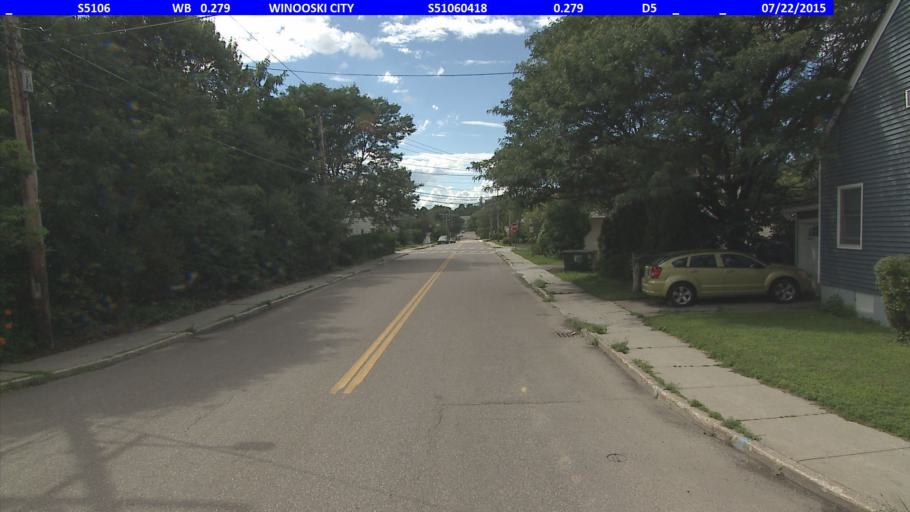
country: US
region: Vermont
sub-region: Chittenden County
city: Winooski
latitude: 44.4954
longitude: -73.1799
